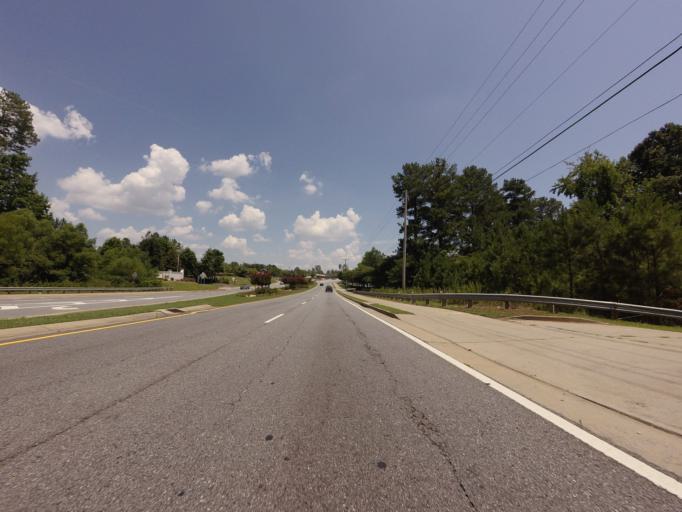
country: US
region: Georgia
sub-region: Fulton County
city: Johns Creek
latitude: 34.0507
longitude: -84.2274
